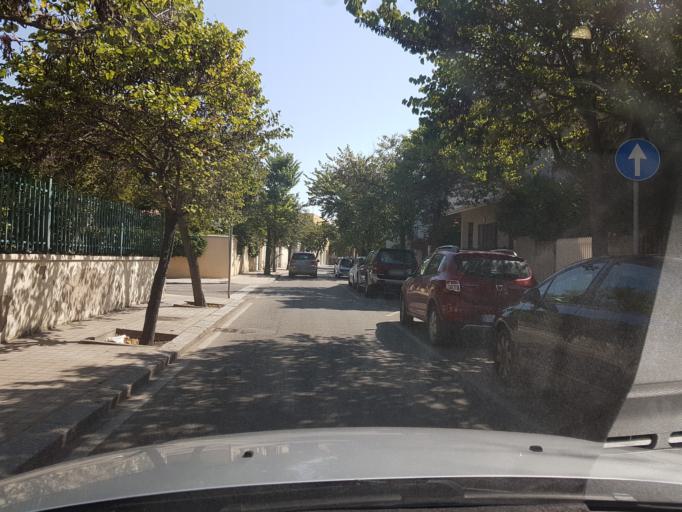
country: IT
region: Sardinia
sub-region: Provincia di Oristano
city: Oristano
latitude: 39.8991
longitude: 8.5889
